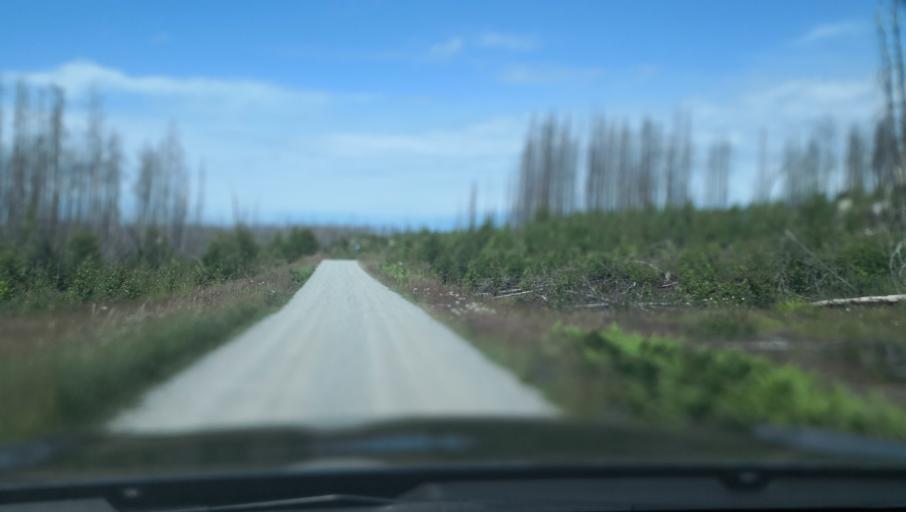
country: SE
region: Vaestmanland
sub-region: Surahammars Kommun
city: Ramnas
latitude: 59.9029
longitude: 16.1448
